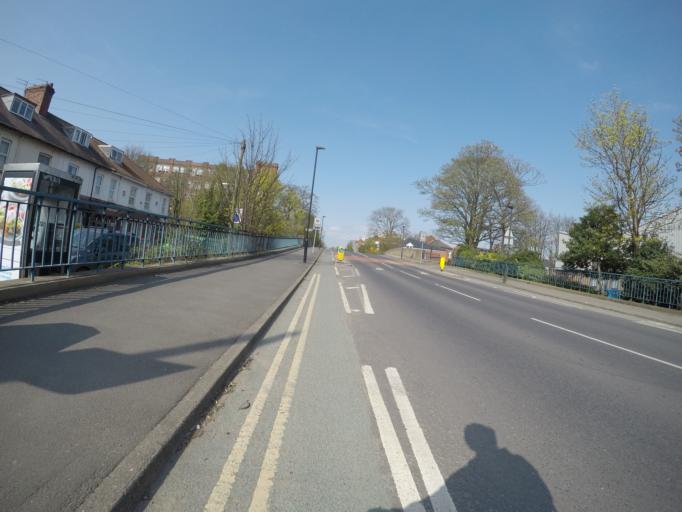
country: GB
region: England
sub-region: City of York
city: York
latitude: 53.9729
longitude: -1.0773
